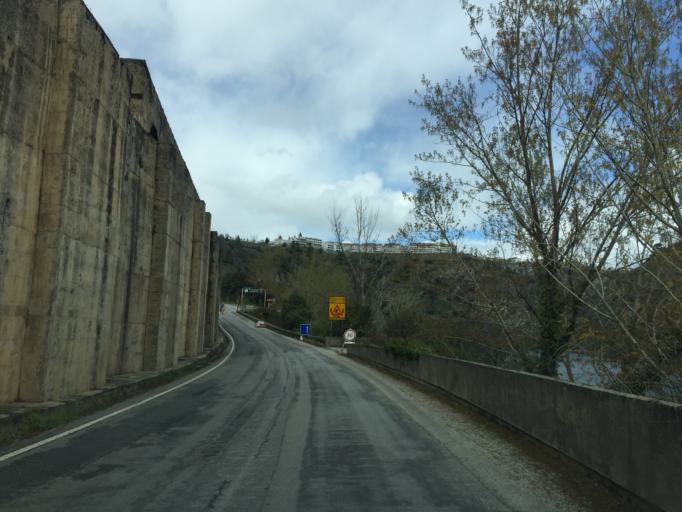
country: PT
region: Braganca
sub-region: Miranda do Douro
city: Miranda do Douro
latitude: 41.4902
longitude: -6.2661
